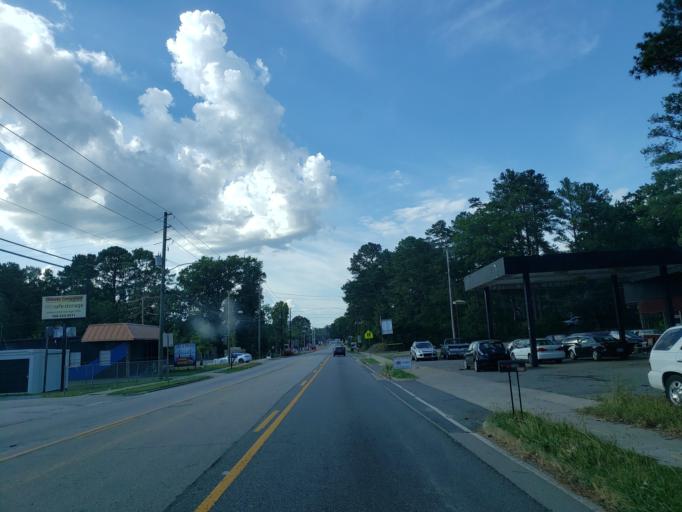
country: US
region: Georgia
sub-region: Floyd County
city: Rome
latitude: 34.2304
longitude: -85.1597
